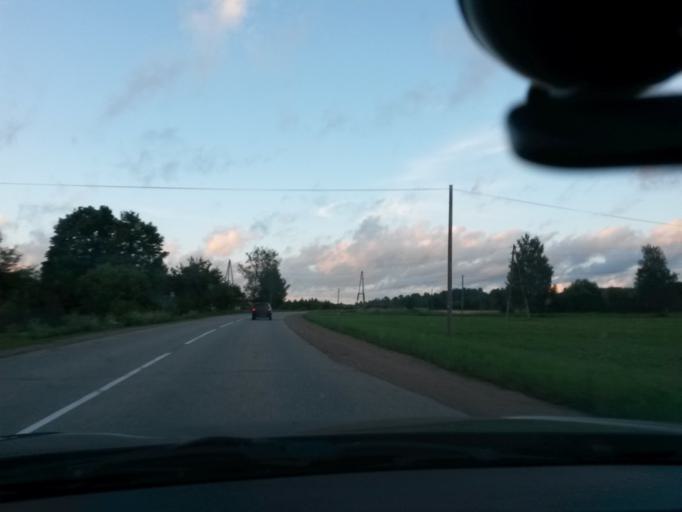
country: LV
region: Madonas Rajons
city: Madona
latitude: 56.7227
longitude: 25.9931
